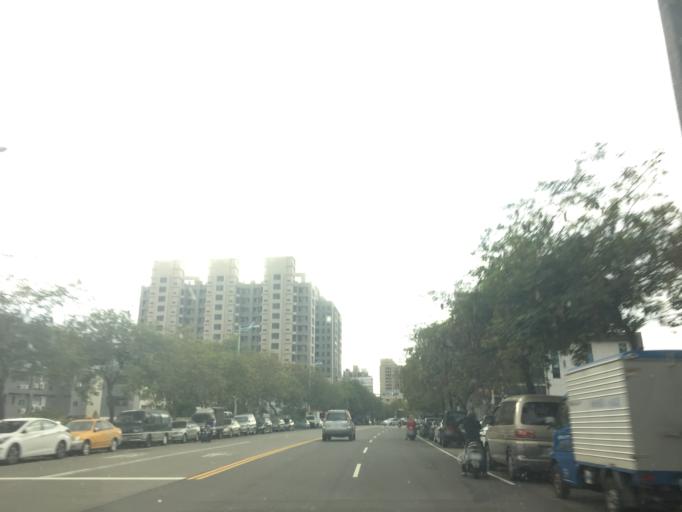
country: TW
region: Taiwan
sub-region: Taichung City
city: Taichung
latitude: 24.1589
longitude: 120.7228
